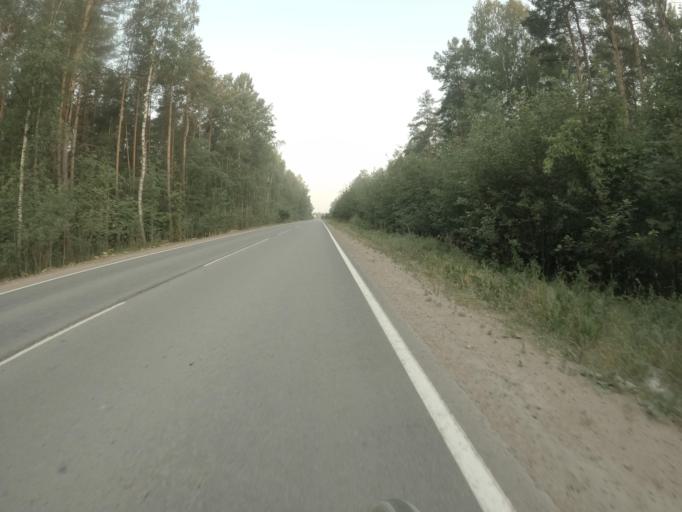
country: RU
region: Leningrad
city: Otradnoye
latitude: 59.7834
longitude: 30.7500
